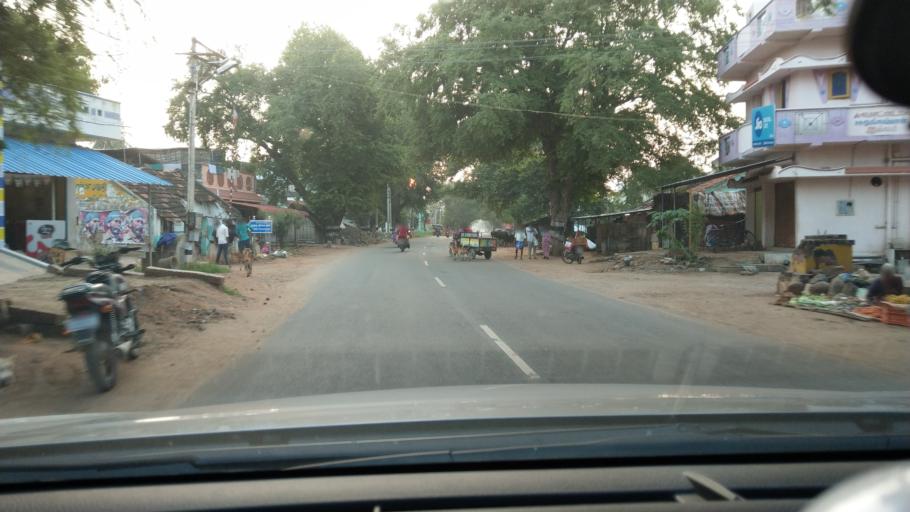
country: IN
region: Tamil Nadu
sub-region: Salem
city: Attur
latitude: 11.5995
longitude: 78.5801
